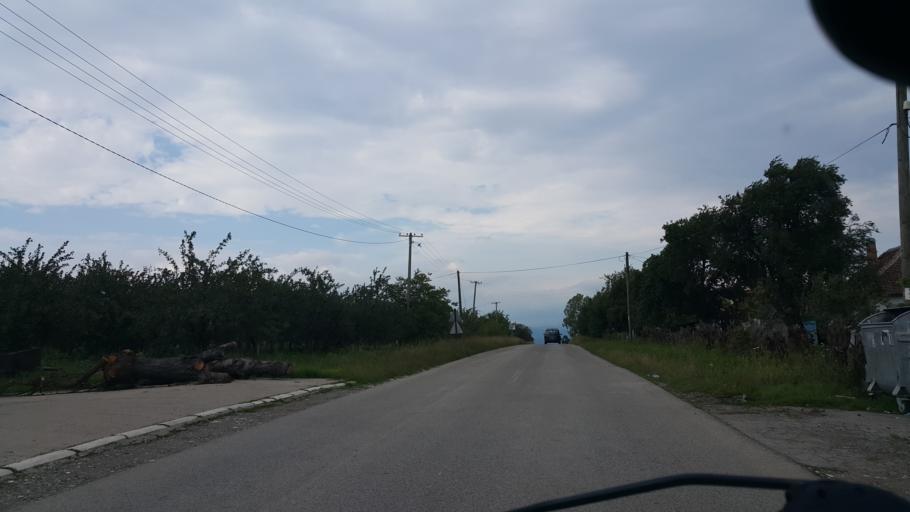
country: RS
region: Central Serbia
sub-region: Toplicki Okrug
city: Blace
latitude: 43.2622
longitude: 21.2712
